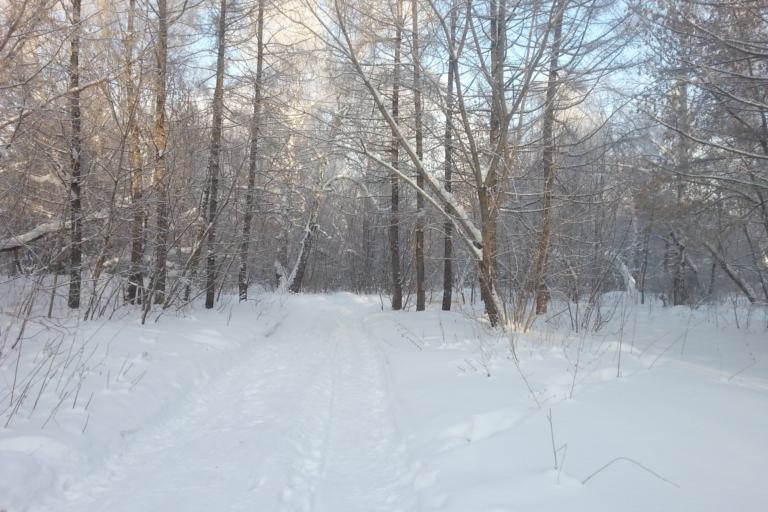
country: RU
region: Altai Krai
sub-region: Gorod Barnaulskiy
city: Barnaul
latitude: 53.3684
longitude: 83.7205
